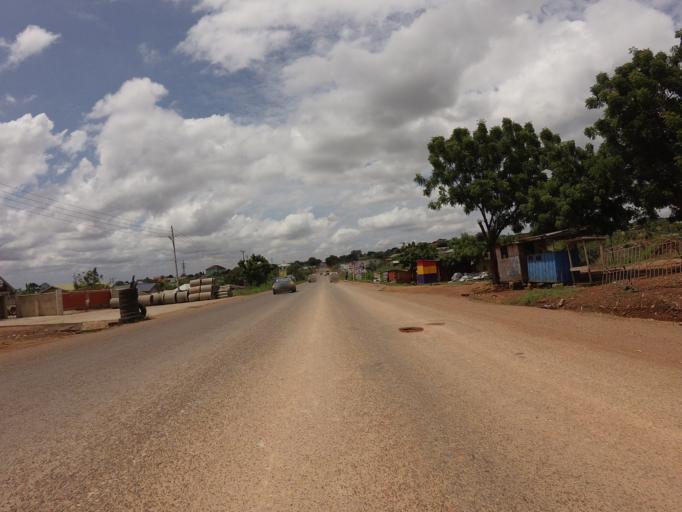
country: GH
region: Eastern
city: Aburi
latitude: 5.8230
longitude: -0.1199
